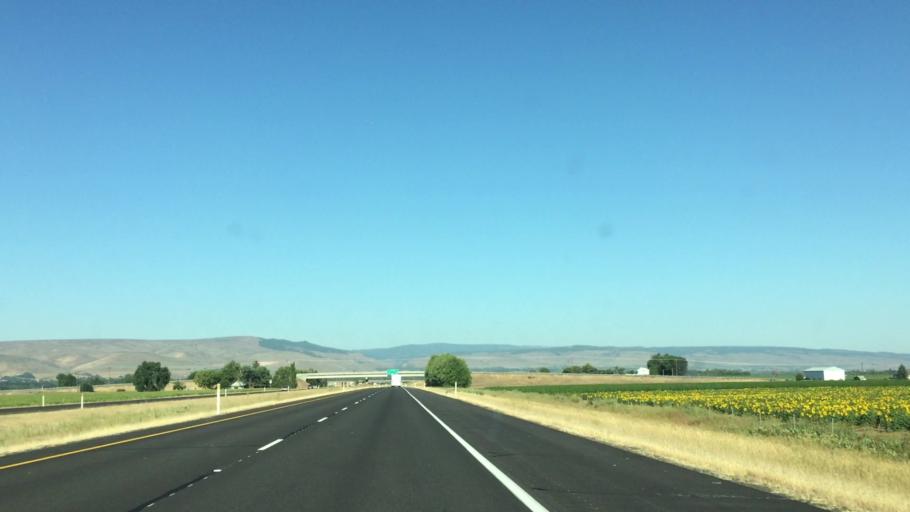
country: US
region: Washington
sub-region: Kittitas County
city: Ellensburg
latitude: 46.9716
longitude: -120.4906
